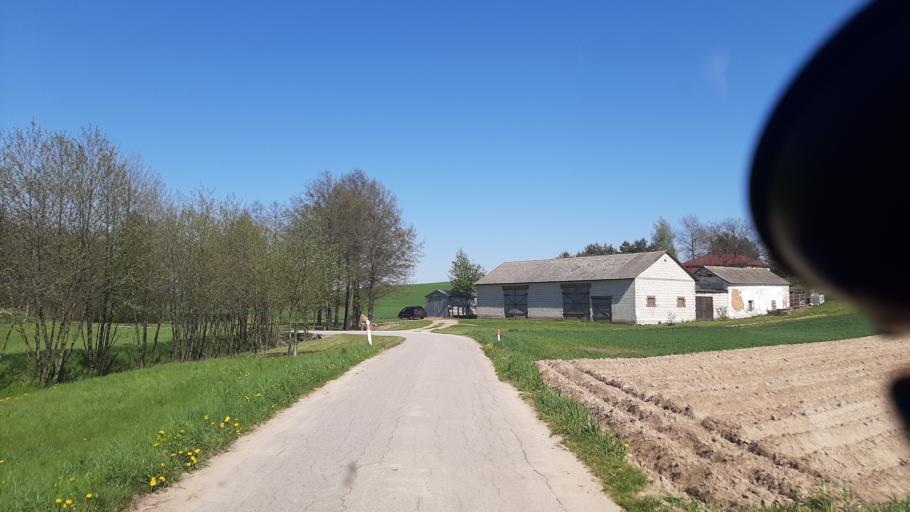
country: PL
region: Lublin Voivodeship
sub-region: Powiat lubelski
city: Jastkow
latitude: 51.3420
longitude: 22.3921
